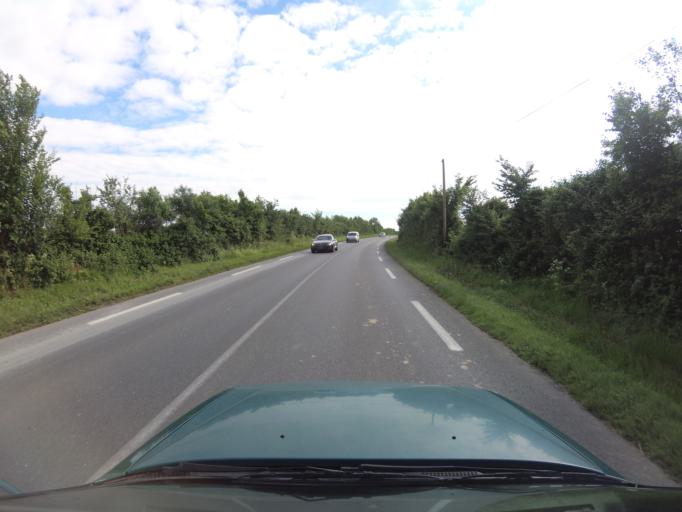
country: FR
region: Poitou-Charentes
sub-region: Departement de la Charente-Maritime
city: Saint-Xandre
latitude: 46.2204
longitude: -1.0864
